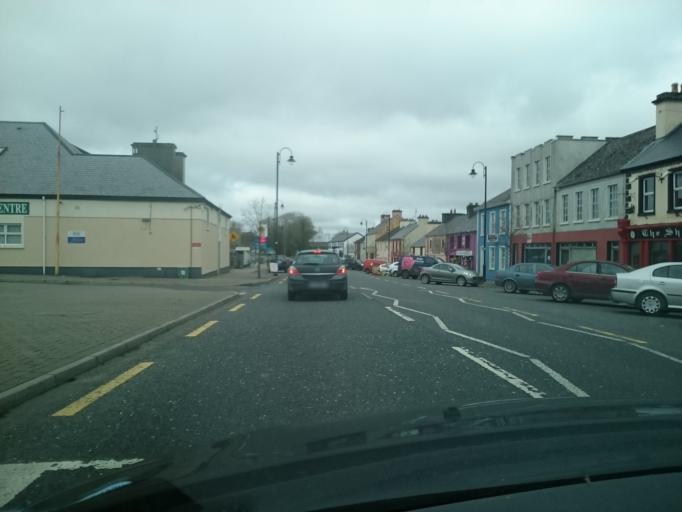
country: IE
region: Connaught
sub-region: Maigh Eo
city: Kiltamagh
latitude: 53.8046
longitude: -9.1306
